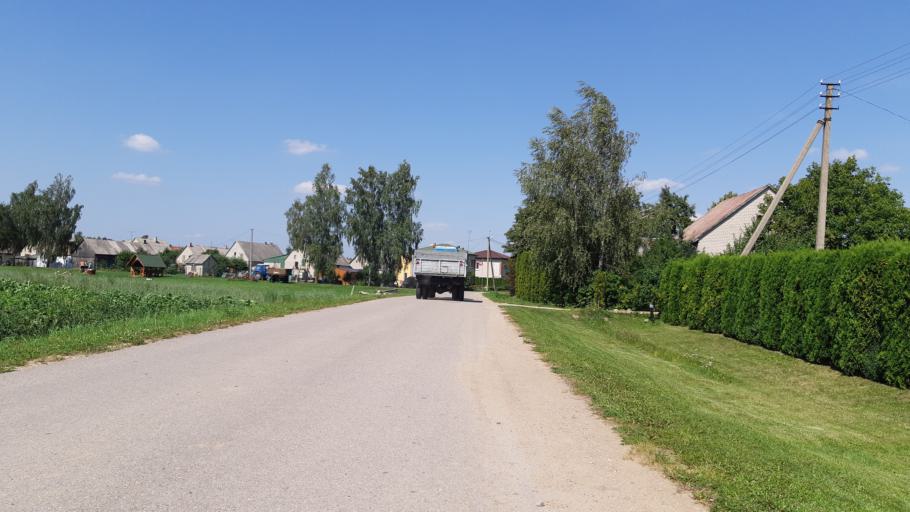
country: LT
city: Virbalis
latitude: 54.6201
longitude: 22.8164
